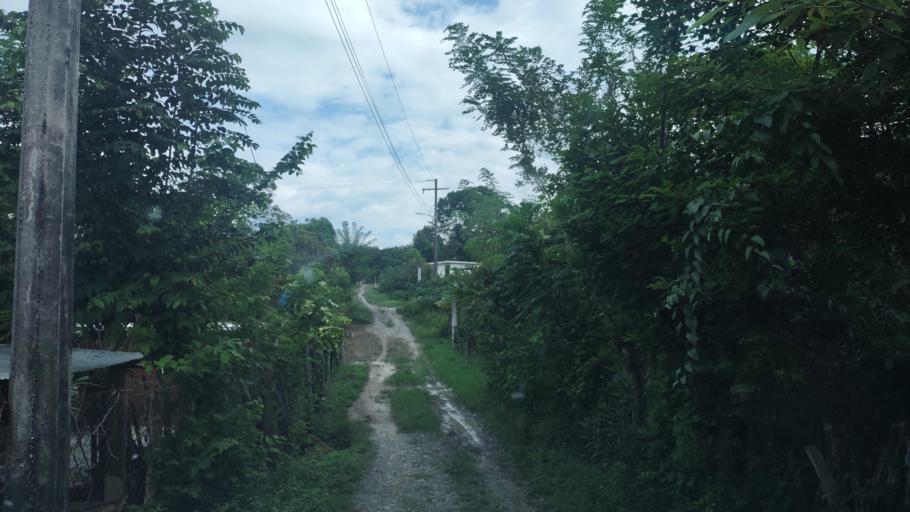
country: MX
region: Veracruz
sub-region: Ixcatepec
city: Ixcatepec
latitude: 21.2139
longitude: -97.9820
